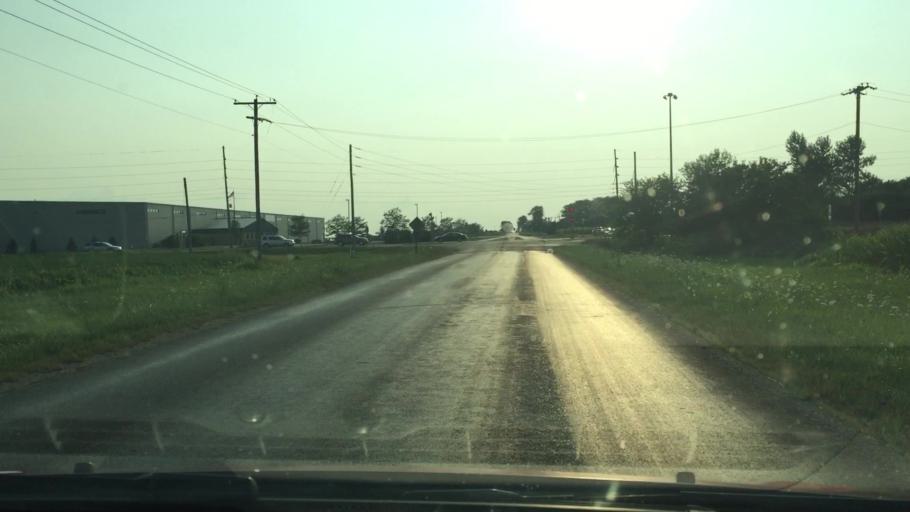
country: US
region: Illinois
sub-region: Bureau County
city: Ladd
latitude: 41.3643
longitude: -89.2173
